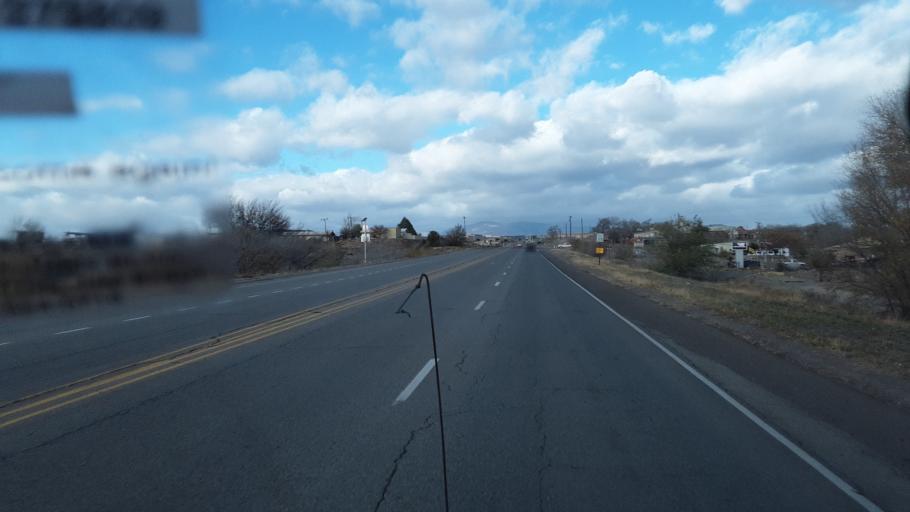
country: US
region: New Mexico
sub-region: Rio Arriba County
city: Espanola
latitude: 36.0083
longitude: -106.0826
